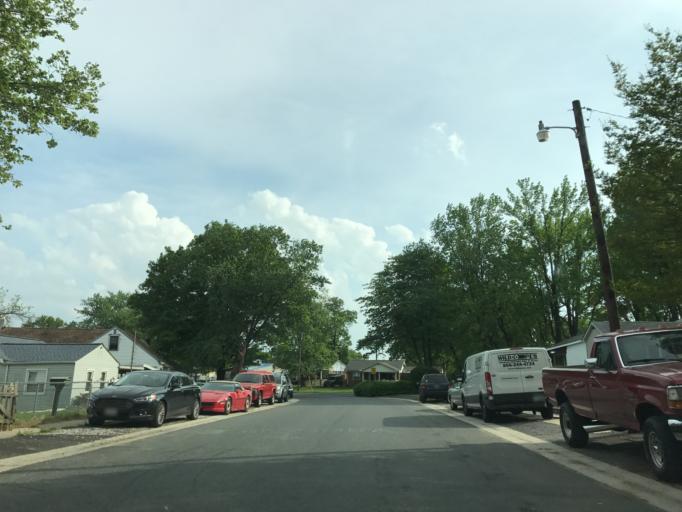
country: US
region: Maryland
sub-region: Baltimore County
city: Middle River
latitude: 39.3320
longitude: -76.4535
